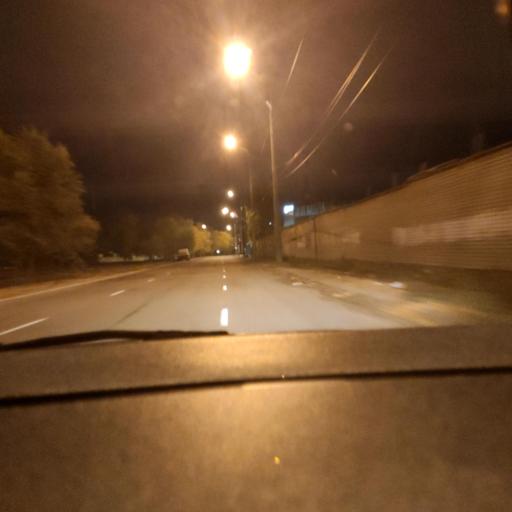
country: RU
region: Voronezj
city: Voronezh
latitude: 51.6777
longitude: 39.1680
